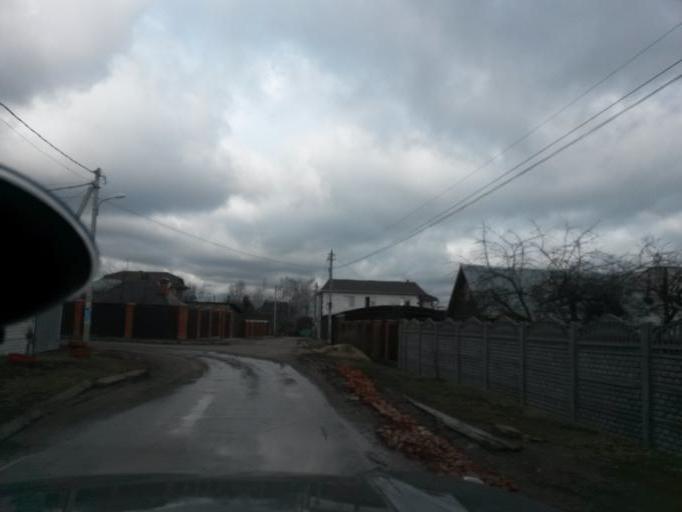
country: RU
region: Moskovskaya
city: Alekseyevka
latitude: 55.6038
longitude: 37.8188
